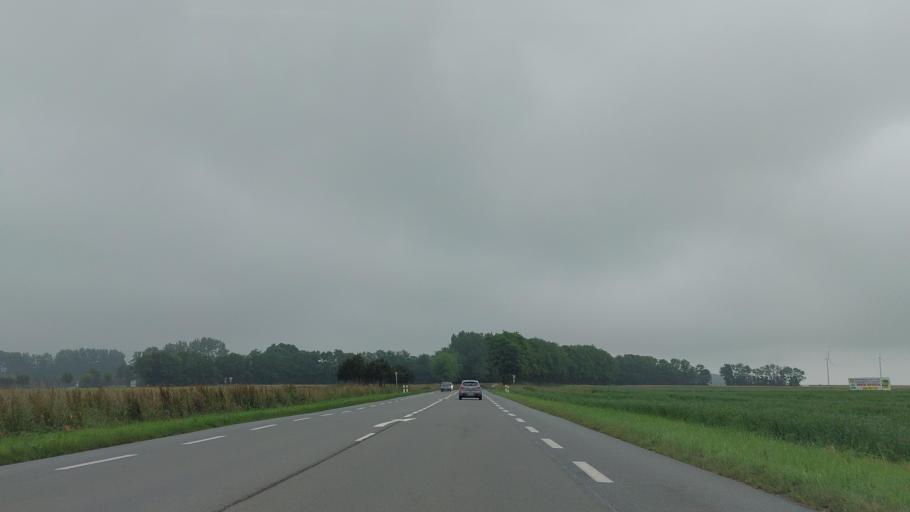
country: FR
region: Picardie
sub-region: Departement de la Somme
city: Bethencourt-sur-Mer
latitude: 50.0696
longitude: 1.5190
